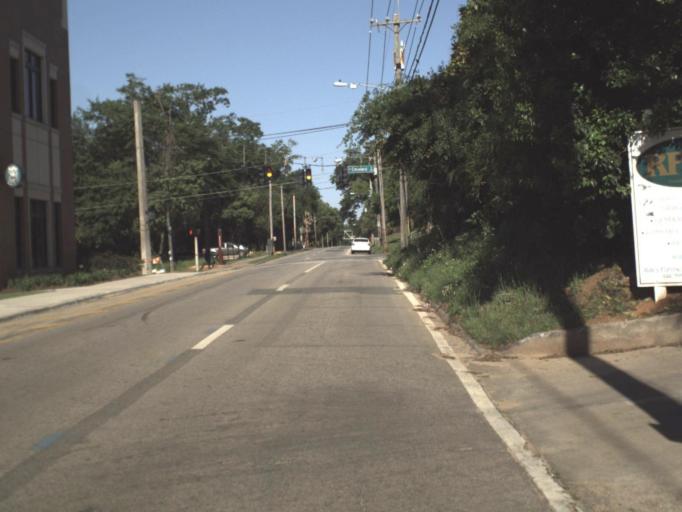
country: US
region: Florida
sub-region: Leon County
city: Tallahassee
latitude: 30.4388
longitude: -84.2901
